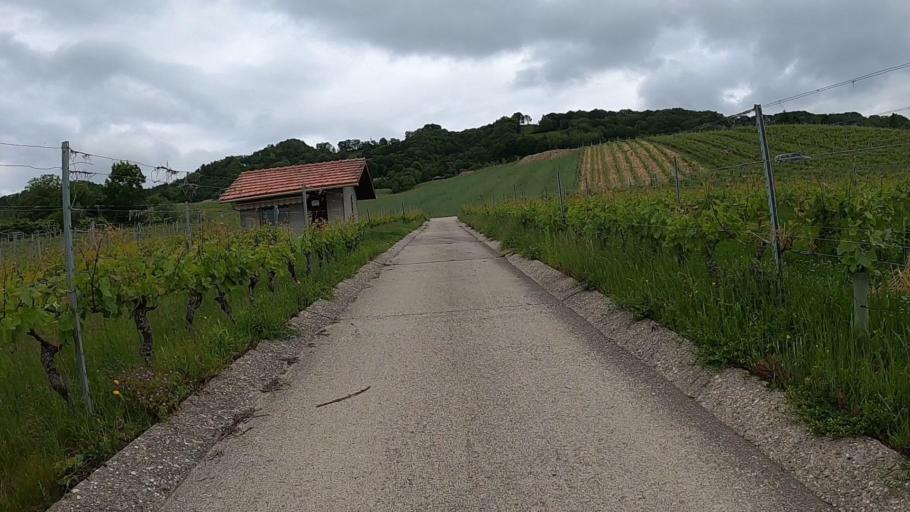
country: CH
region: Vaud
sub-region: Nyon District
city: Rolle
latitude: 46.4706
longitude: 6.3273
